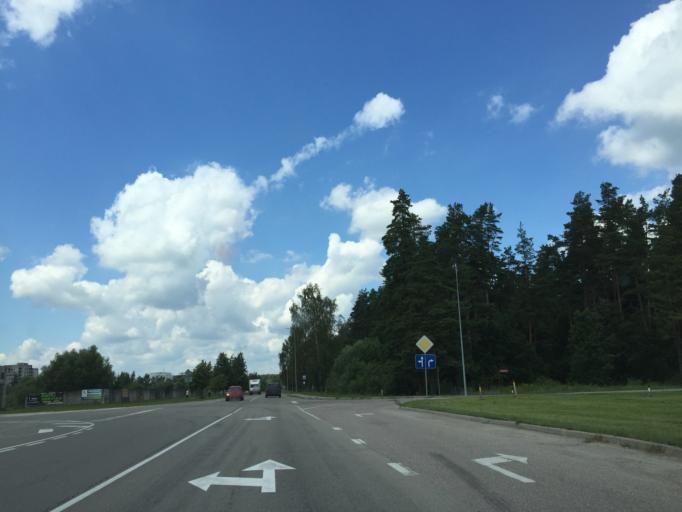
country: LV
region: Ozolnieku
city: Ozolnieki
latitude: 56.6666
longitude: 23.7720
